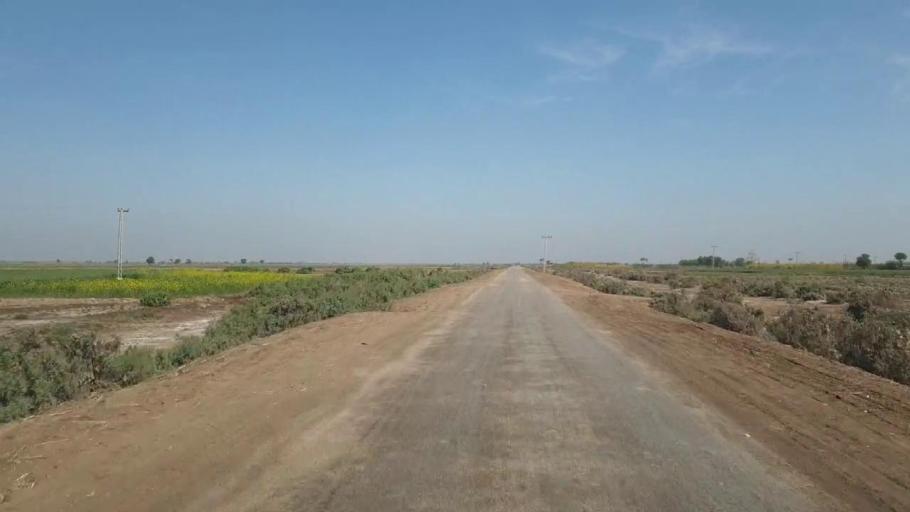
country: PK
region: Sindh
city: Samaro
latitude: 25.3458
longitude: 69.2493
